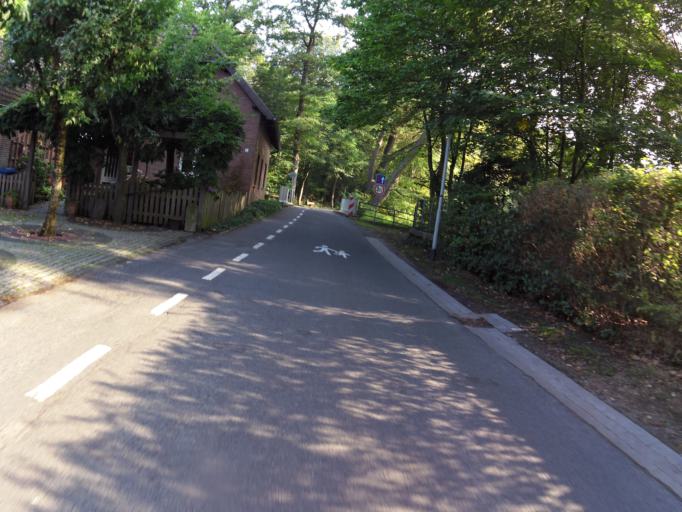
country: DE
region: Lower Saxony
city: Verden
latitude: 52.9431
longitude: 9.2292
